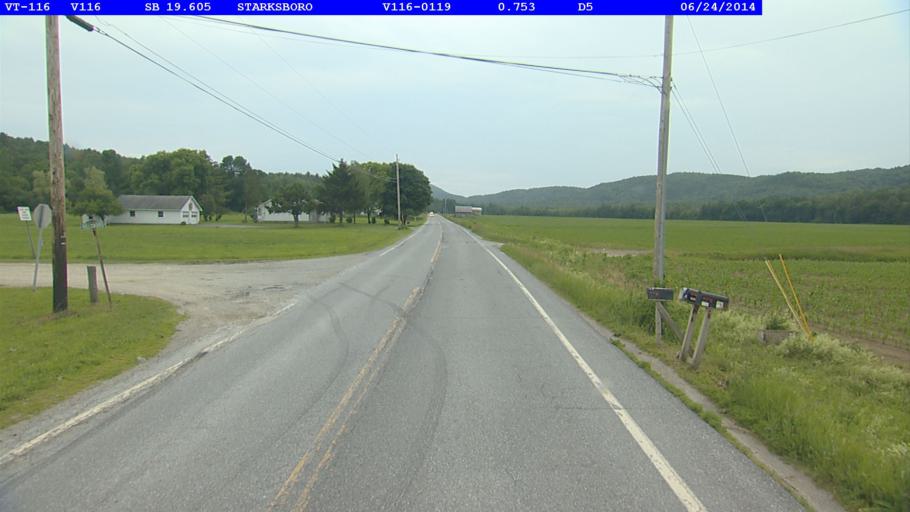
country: US
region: Vermont
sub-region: Addison County
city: Bristol
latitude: 44.1961
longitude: -73.0531
